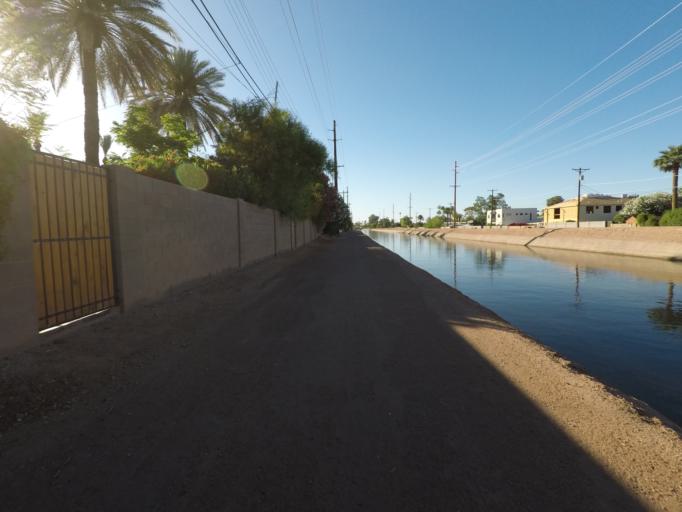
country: US
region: Arizona
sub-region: Maricopa County
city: Paradise Valley
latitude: 33.4997
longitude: -111.9817
